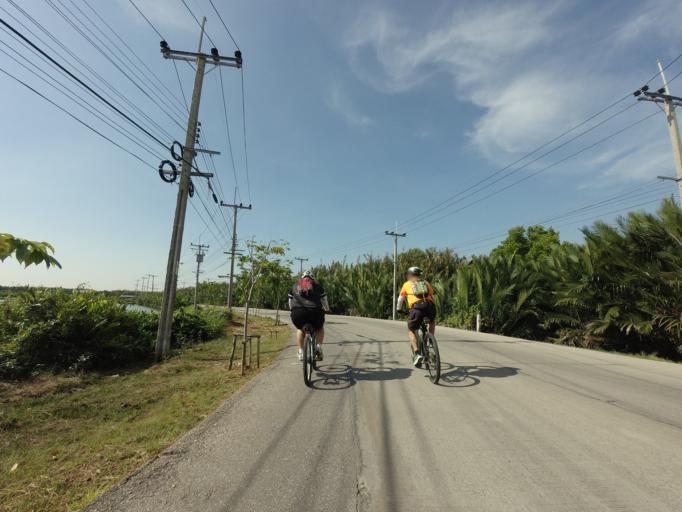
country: TH
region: Samut Prakan
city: Phra Samut Chedi
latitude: 13.5611
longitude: 100.5431
